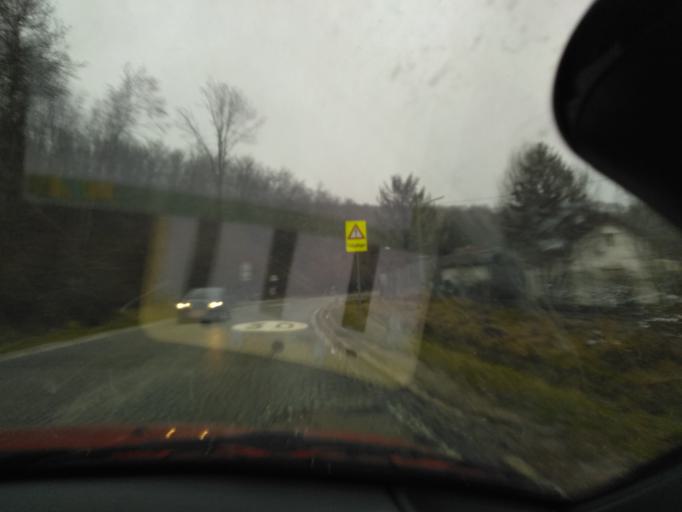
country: AT
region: Lower Austria
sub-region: Politischer Bezirk Wien-Umgebung
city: Klosterneuburg
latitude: 48.2525
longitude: 16.2735
